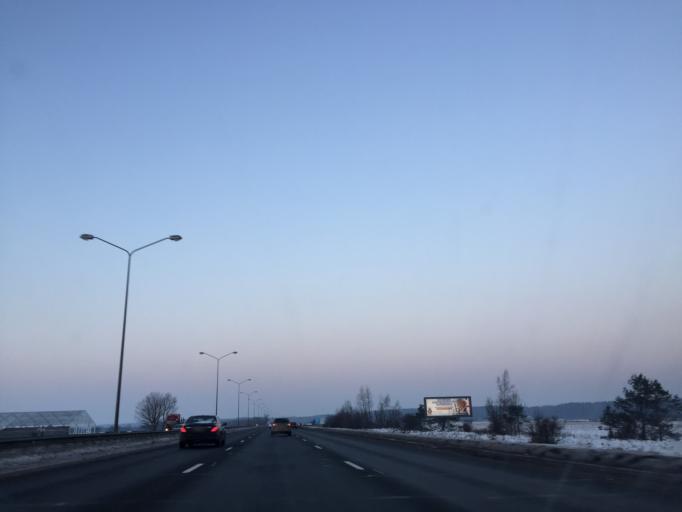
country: LV
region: Babite
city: Pinki
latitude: 56.9583
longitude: 23.9014
